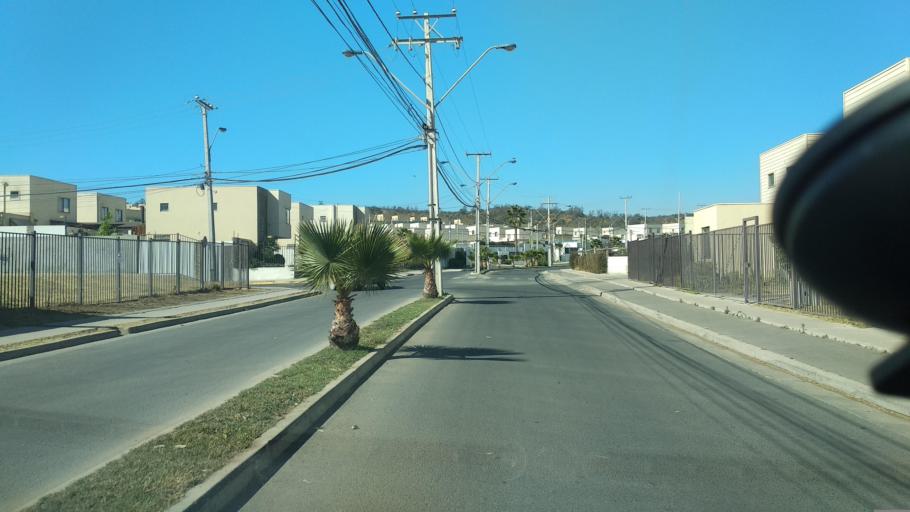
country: CL
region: Valparaiso
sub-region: Provincia de Marga Marga
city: Villa Alemana
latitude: -33.0356
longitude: -71.3878
